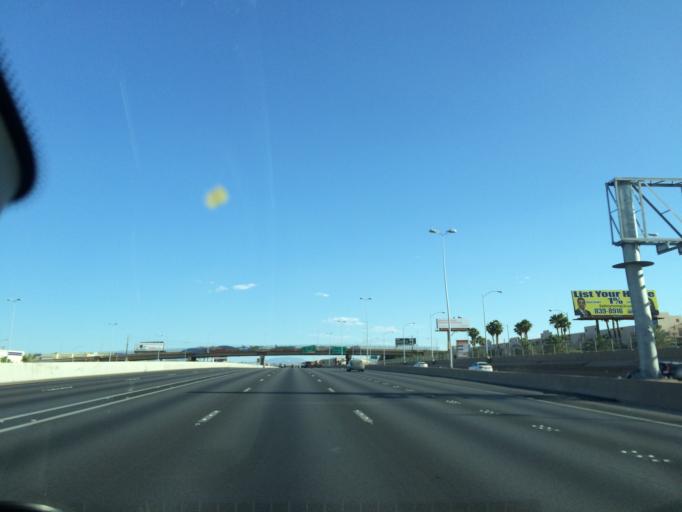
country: US
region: Nevada
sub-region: Clark County
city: Paradise
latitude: 36.0740
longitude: -115.1809
